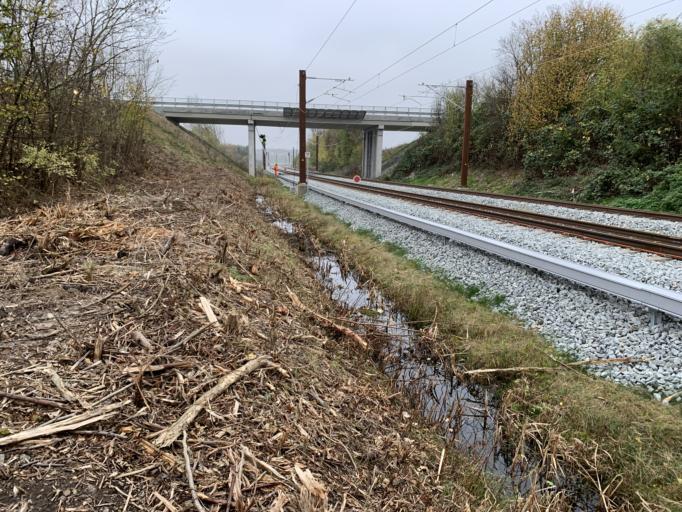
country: DK
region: Zealand
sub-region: Ringsted Kommune
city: Ringsted
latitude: 55.3925
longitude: 11.7370
